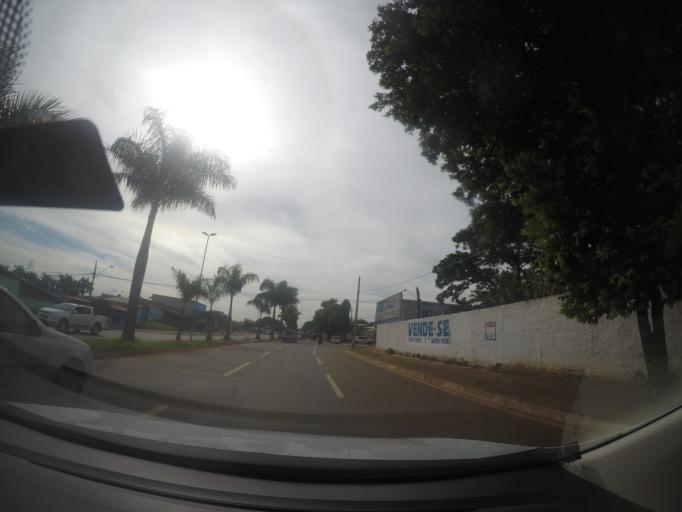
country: BR
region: Goias
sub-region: Goiania
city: Goiania
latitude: -16.6563
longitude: -49.2989
